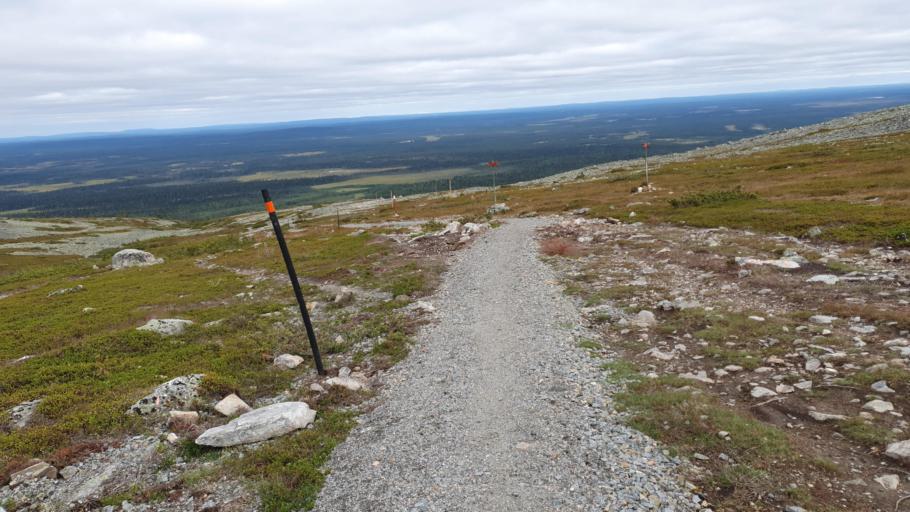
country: FI
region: Lapland
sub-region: Tunturi-Lappi
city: Kolari
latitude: 67.5684
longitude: 24.2395
